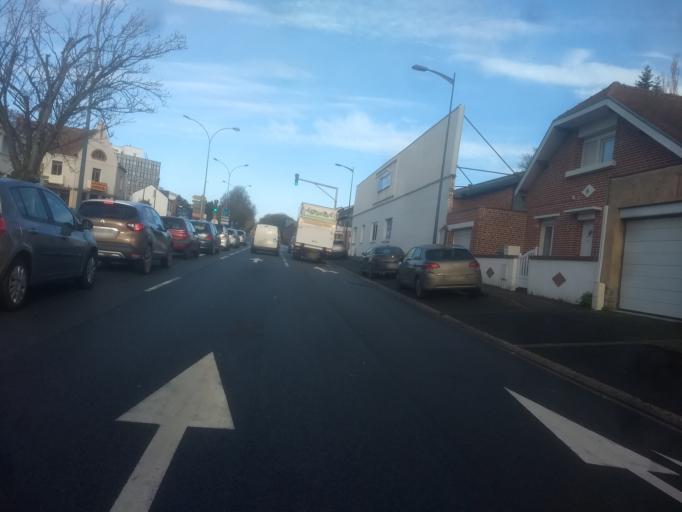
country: FR
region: Nord-Pas-de-Calais
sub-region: Departement du Pas-de-Calais
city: Achicourt
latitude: 50.2889
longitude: 2.7603
